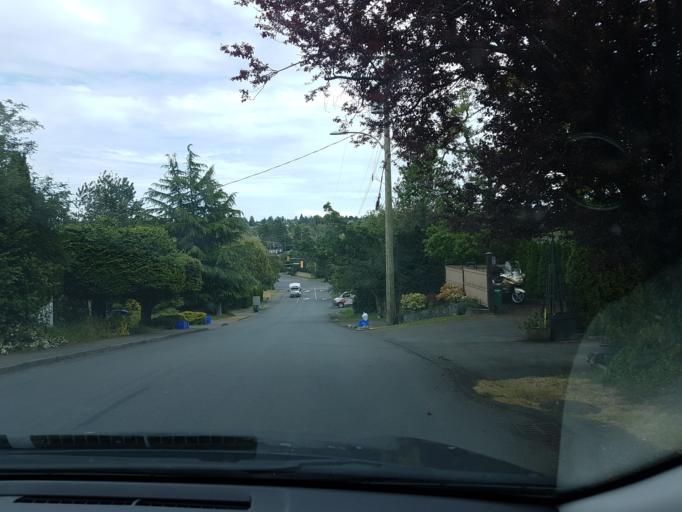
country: CA
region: British Columbia
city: Oak Bay
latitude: 48.4841
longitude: -123.3390
